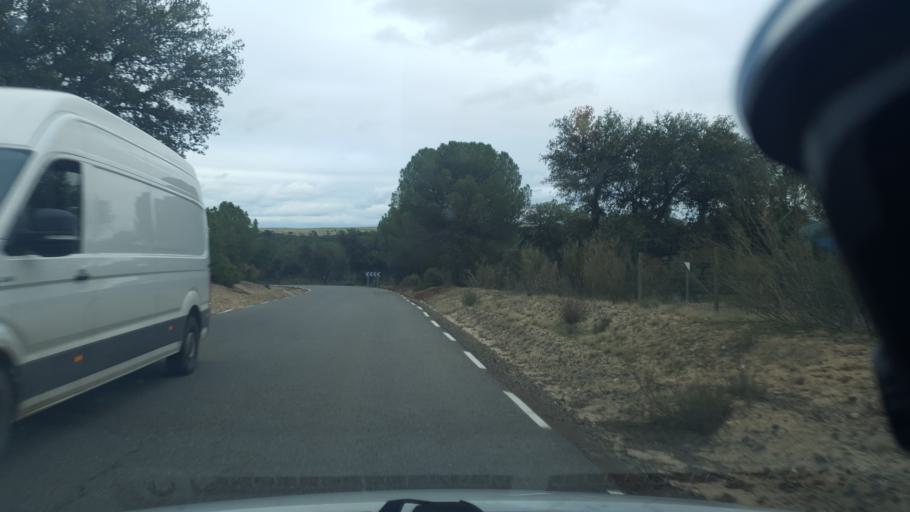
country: ES
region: Castille and Leon
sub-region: Provincia de Avila
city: Pozanco
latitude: 40.8265
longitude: -4.6957
